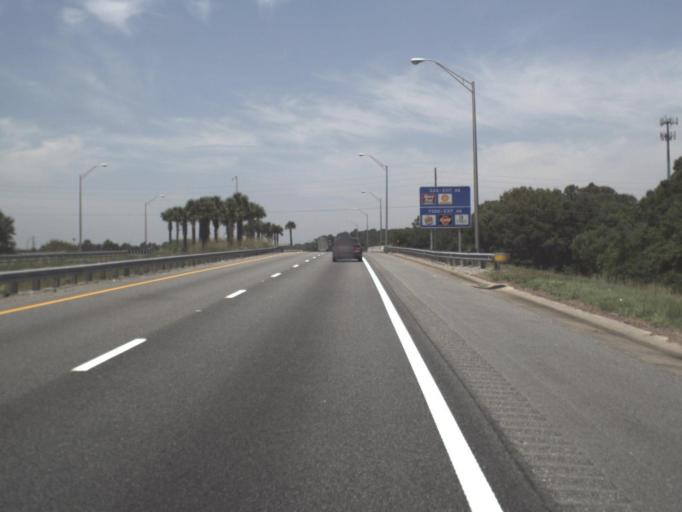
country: US
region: Florida
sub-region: Duval County
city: Jacksonville
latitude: 30.3400
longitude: -81.5405
